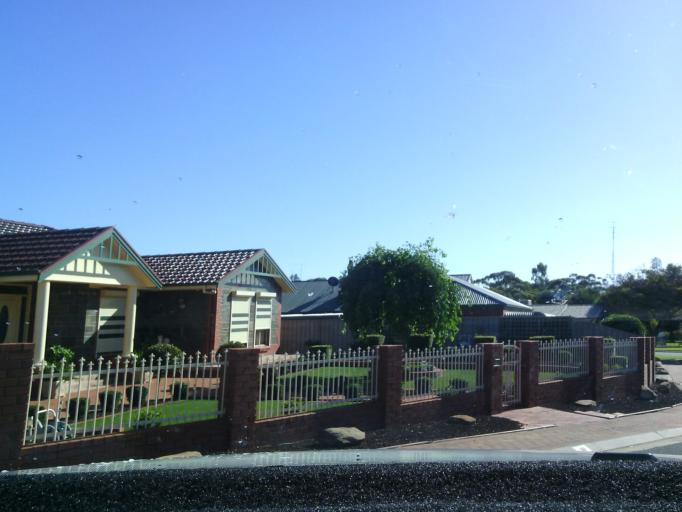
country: AU
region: South Australia
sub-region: Berri and Barmera
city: Berri
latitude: -34.2805
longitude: 140.6011
